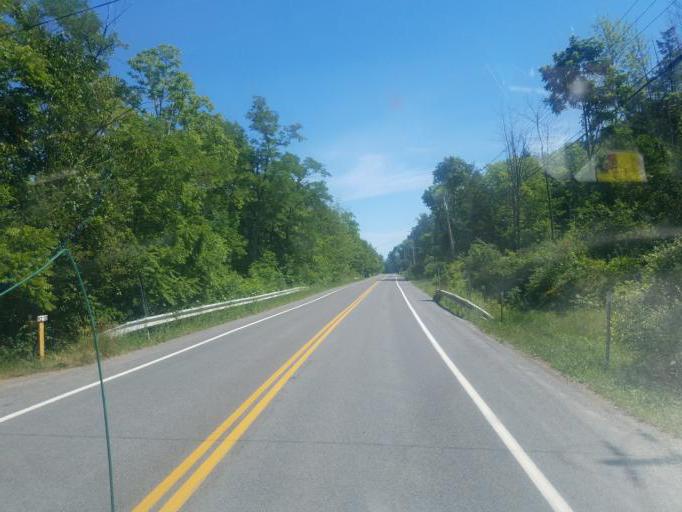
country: US
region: New York
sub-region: Ontario County
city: Canandaigua
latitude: 42.7748
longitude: -77.2943
